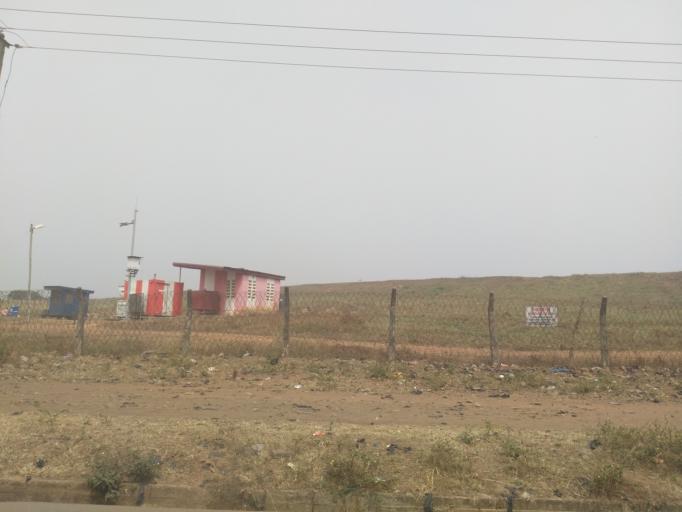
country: GH
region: Ashanti
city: Kumasi
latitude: 6.7024
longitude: -1.5925
